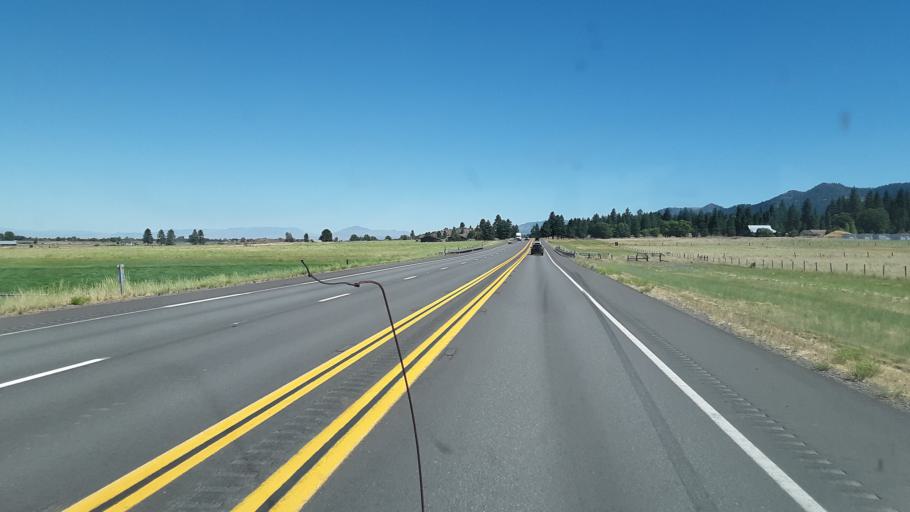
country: US
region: California
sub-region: Lassen County
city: Janesville
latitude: 40.3121
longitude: -120.5361
